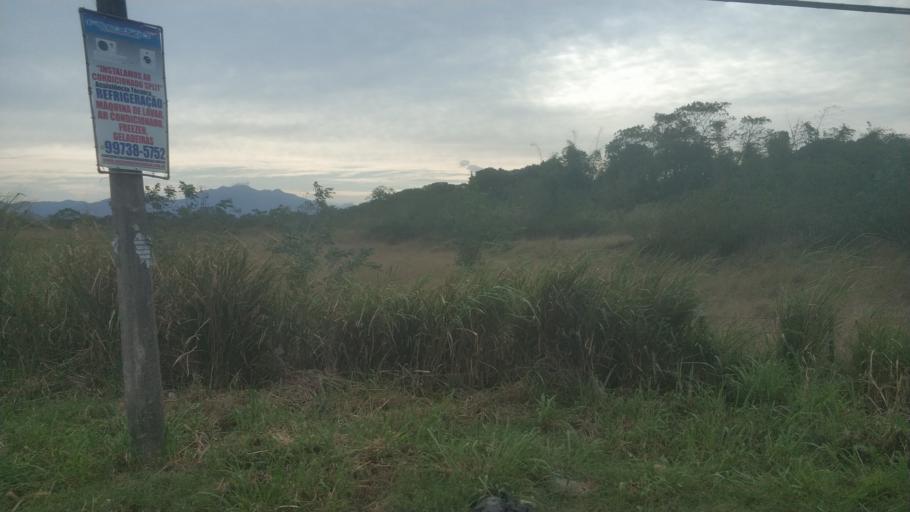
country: BR
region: Rio de Janeiro
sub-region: Seropedica
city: Seropedica
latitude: -22.7945
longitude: -43.6486
